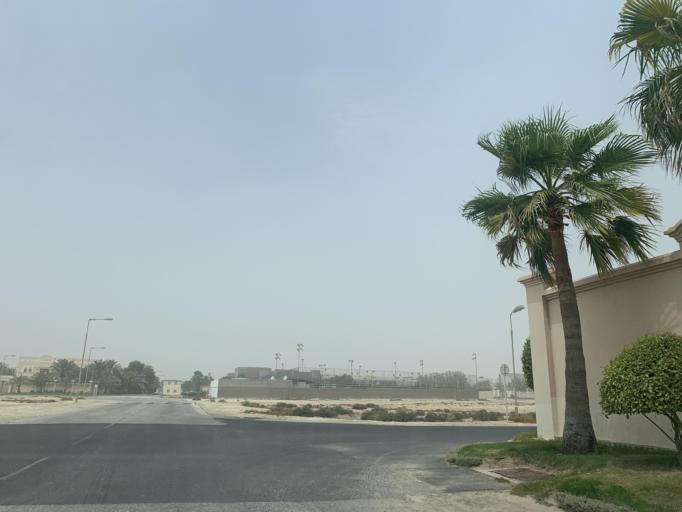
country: BH
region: Central Governorate
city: Madinat Hamad
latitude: 26.1664
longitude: 50.4766
